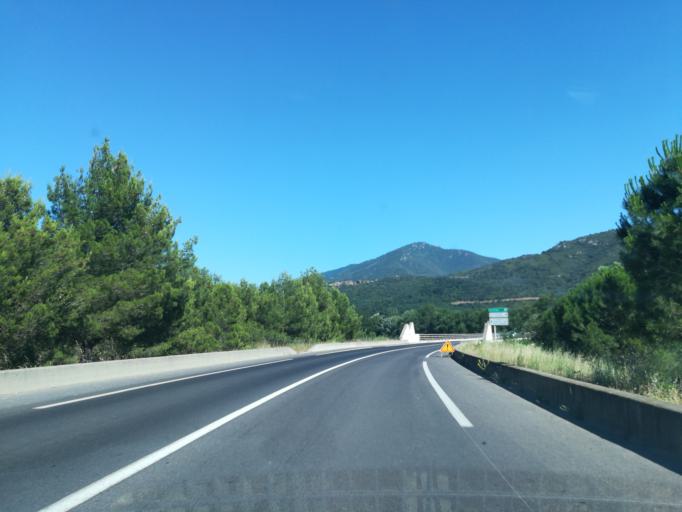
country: FR
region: Languedoc-Roussillon
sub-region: Departement des Pyrenees-Orientales
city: el Volo
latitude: 42.5198
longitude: 2.8263
